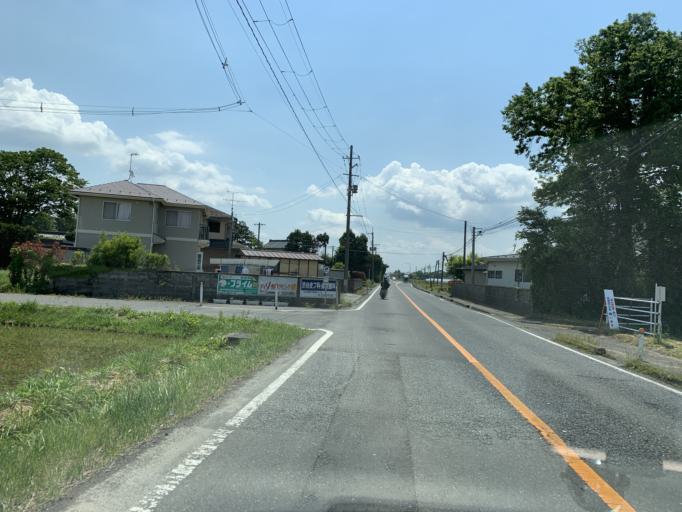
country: JP
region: Miyagi
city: Kogota
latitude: 38.5695
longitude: 141.0412
